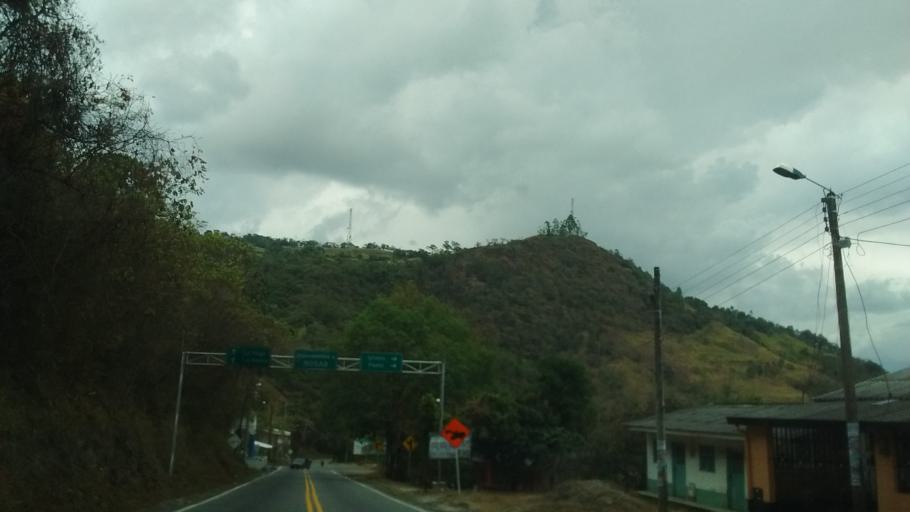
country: CO
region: Cauca
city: Rosas
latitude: 2.2636
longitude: -76.7388
